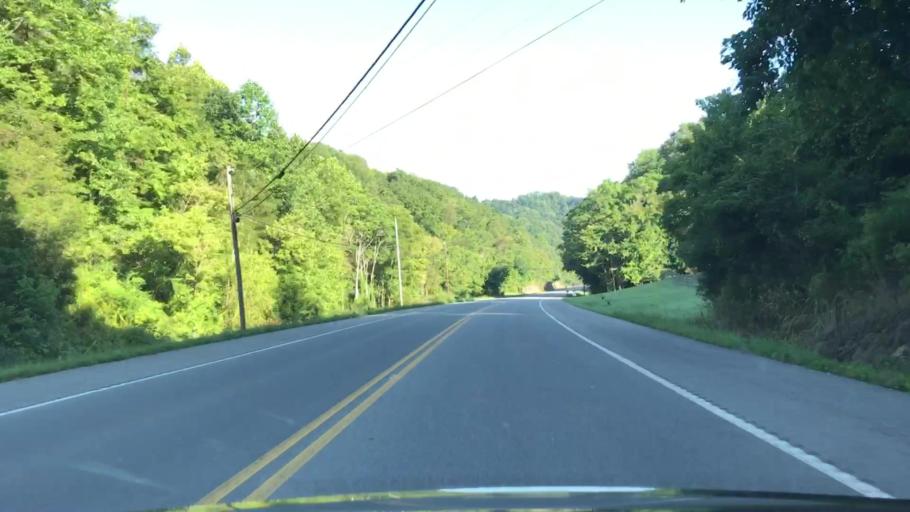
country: US
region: Tennessee
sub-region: Jackson County
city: Gainesboro
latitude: 36.3180
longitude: -85.6538
